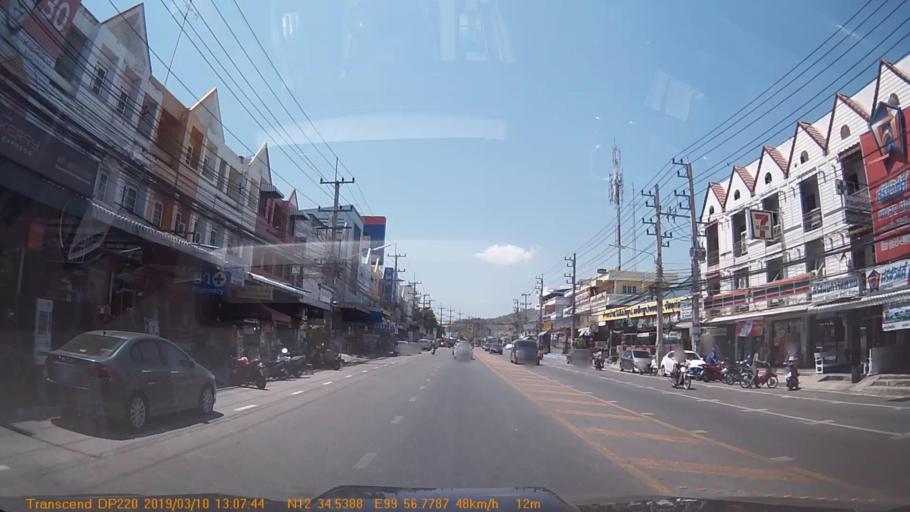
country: TH
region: Prachuap Khiri Khan
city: Hua Hin
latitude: 12.5757
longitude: 99.9462
